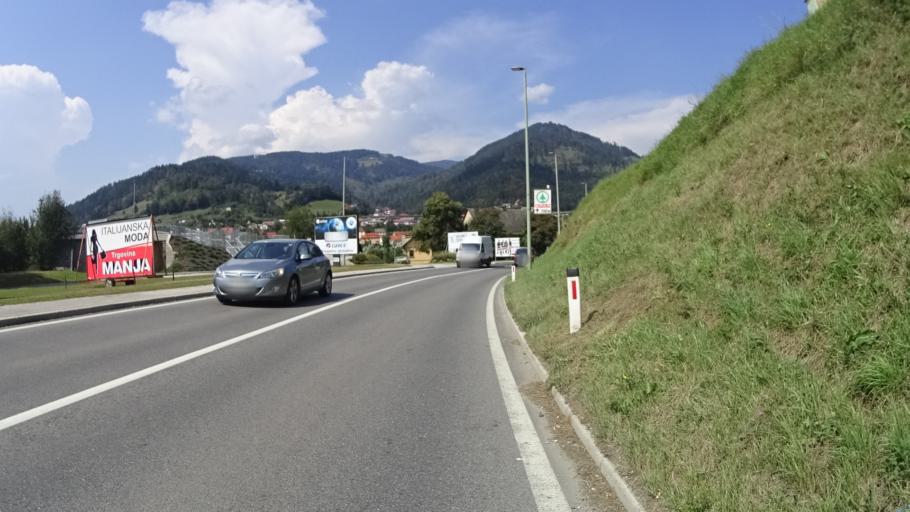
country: SI
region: Dravograd
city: Dravograd
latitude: 46.5844
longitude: 15.0230
